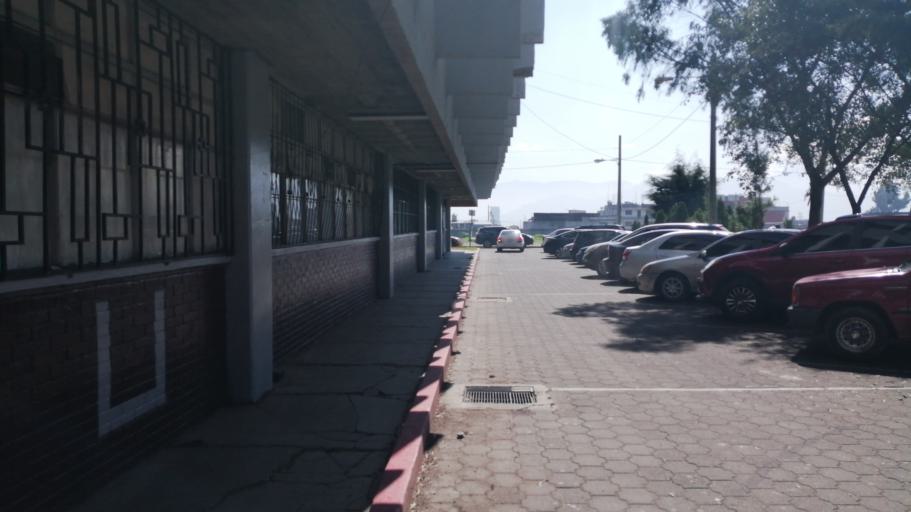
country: GT
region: Quetzaltenango
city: Quetzaltenango
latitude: 14.8447
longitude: -91.5352
